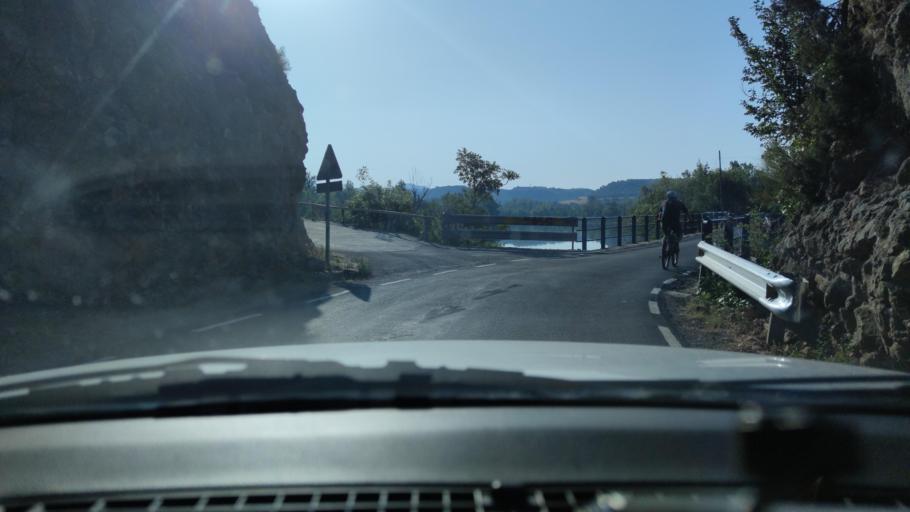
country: ES
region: Catalonia
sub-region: Provincia de Lleida
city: Camarasa
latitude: 41.8722
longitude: 0.8575
